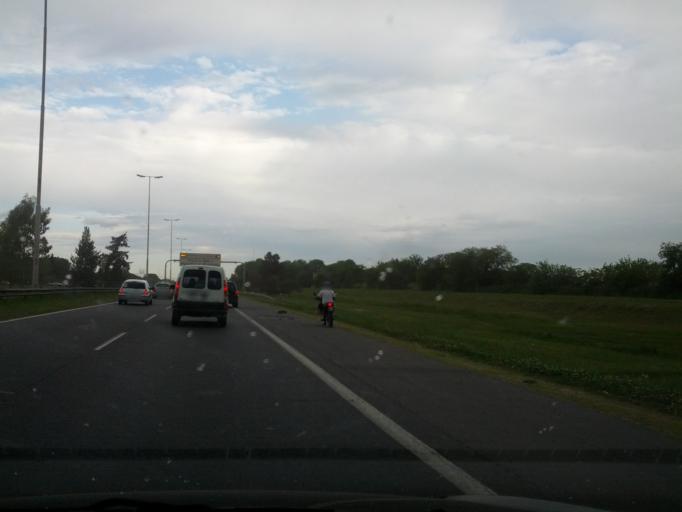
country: AR
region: Buenos Aires
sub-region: Partido de General Rodriguez
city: General Rodriguez
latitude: -34.5764
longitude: -59.0253
